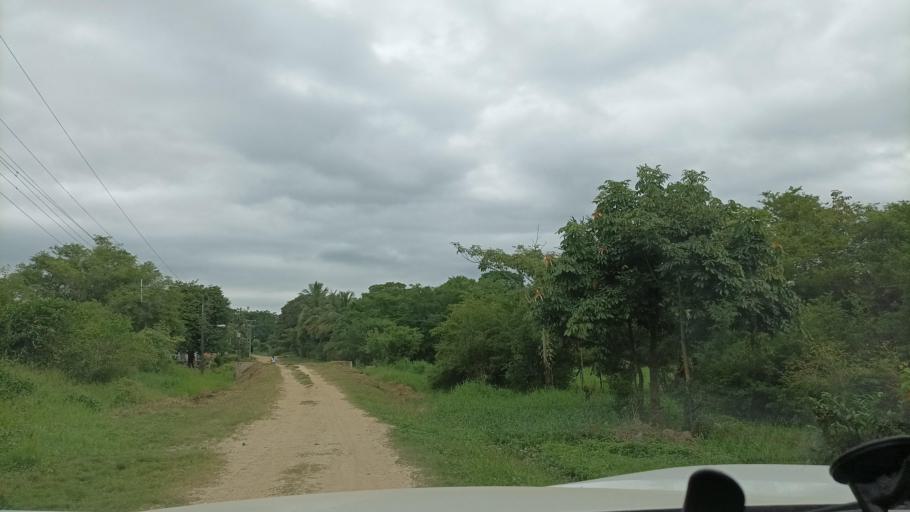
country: MX
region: Veracruz
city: Hidalgotitlan
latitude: 17.8069
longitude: -94.5393
